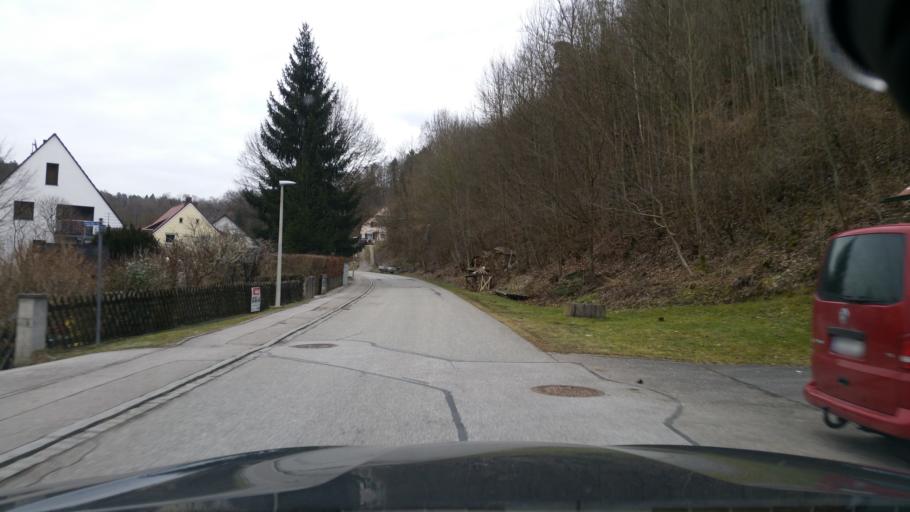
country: DE
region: Bavaria
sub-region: Lower Bavaria
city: Tiefenbach
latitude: 48.5144
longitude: 12.1050
